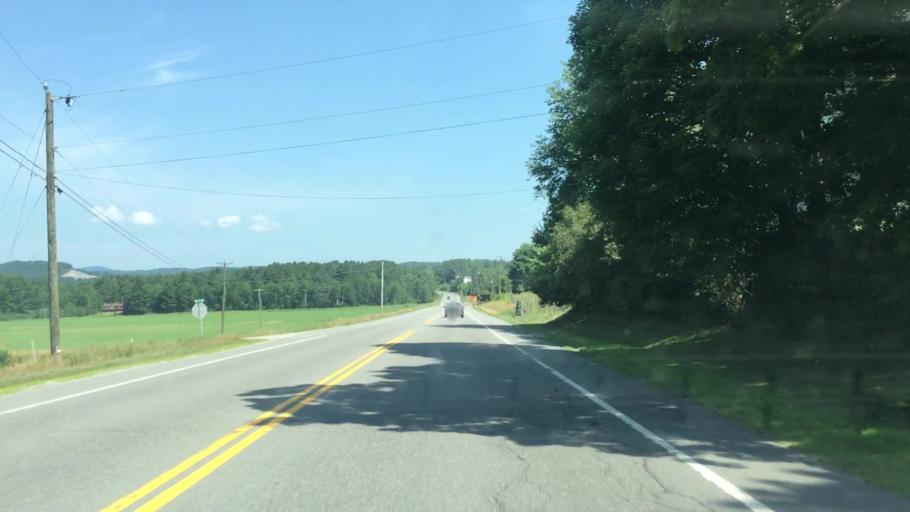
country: US
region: New Hampshire
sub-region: Sullivan County
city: Sunapee
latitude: 43.3628
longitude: -72.1202
